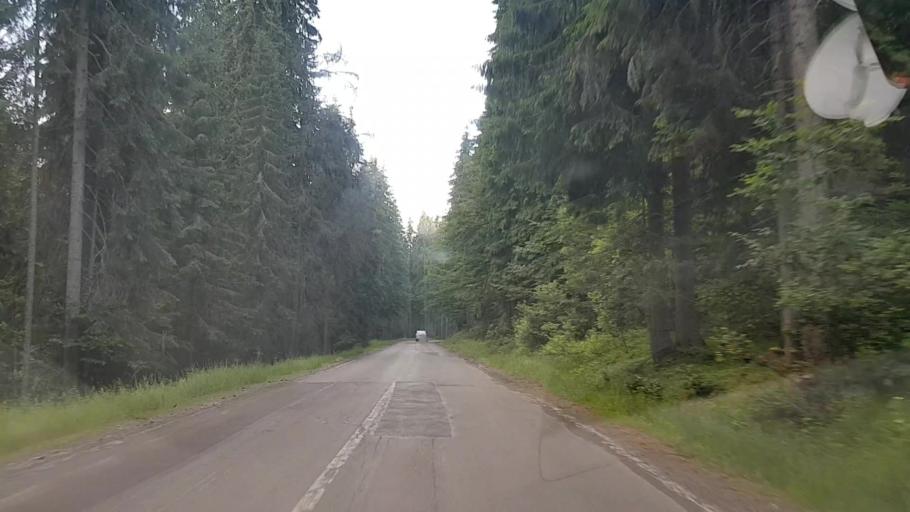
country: RO
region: Harghita
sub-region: Comuna Varsag
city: Varsag
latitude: 46.6515
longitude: 25.2903
